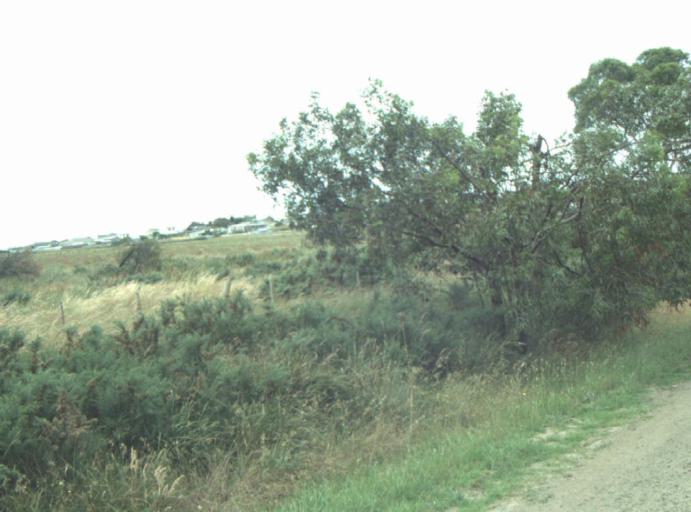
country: AU
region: Victoria
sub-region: Queenscliffe
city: Queenscliff
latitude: -38.1366
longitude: 144.6990
